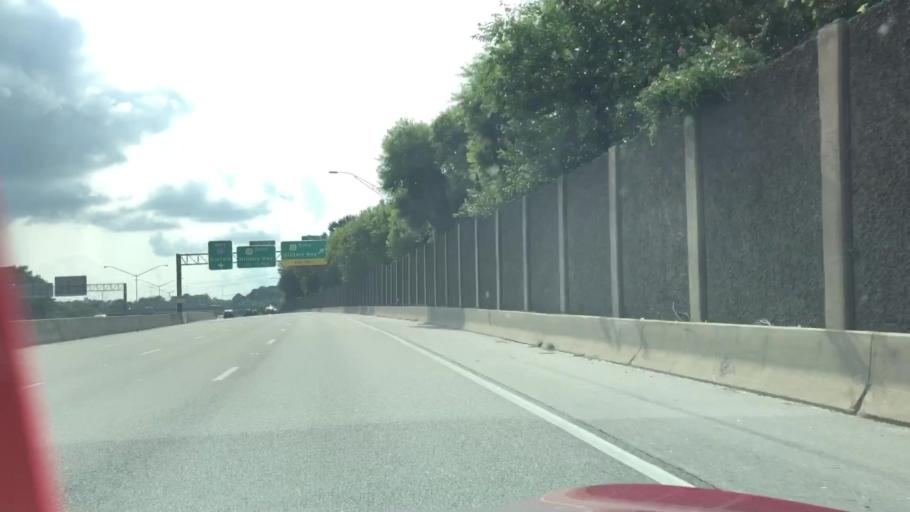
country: US
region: Virginia
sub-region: City of Chesapeake
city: Chesapeake
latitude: 36.8451
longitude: -76.2049
